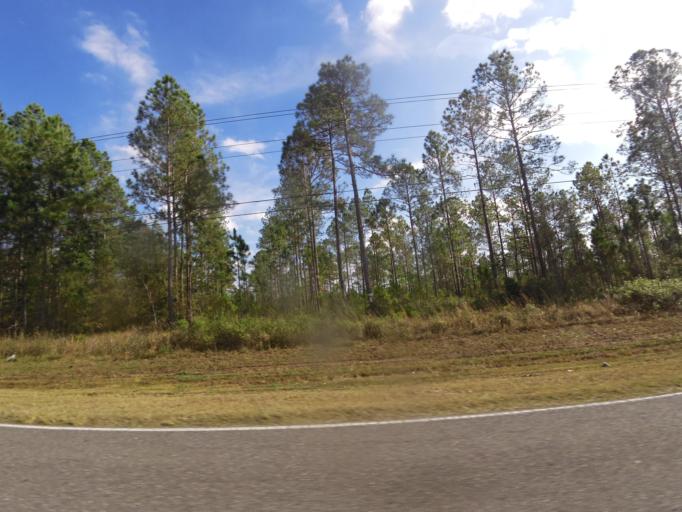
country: US
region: Florida
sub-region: Duval County
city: Baldwin
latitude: 30.1719
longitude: -81.9949
